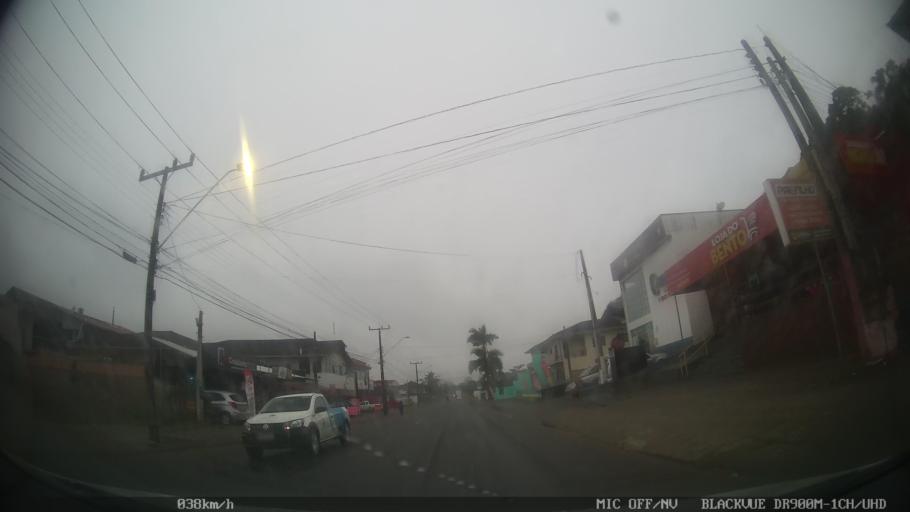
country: BR
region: Santa Catarina
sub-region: Joinville
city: Joinville
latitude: -26.2143
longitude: -48.8220
